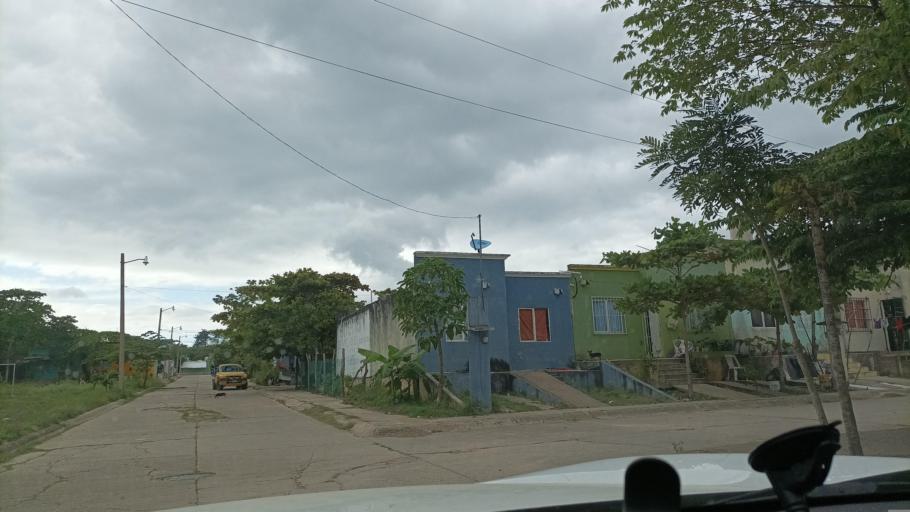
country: MX
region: Veracruz
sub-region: Soconusco
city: Fraccionamiento Santa Cruz
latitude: 17.9708
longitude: -94.8958
